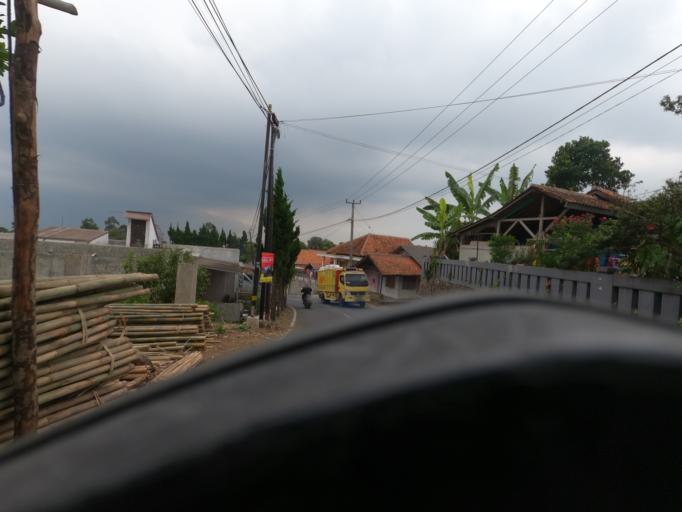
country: ID
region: West Java
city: Cimahi
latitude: -6.8159
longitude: 107.5445
